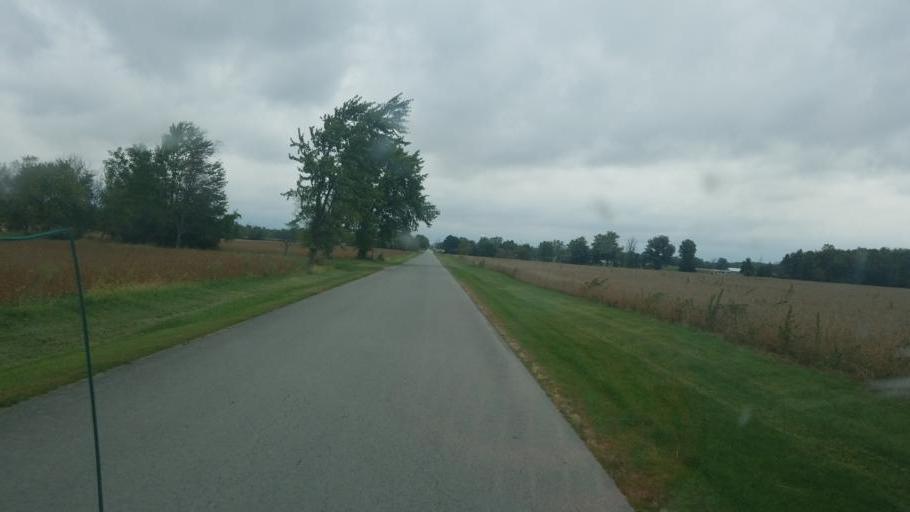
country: US
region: Ohio
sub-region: Seneca County
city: Fostoria
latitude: 41.0969
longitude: -83.5165
